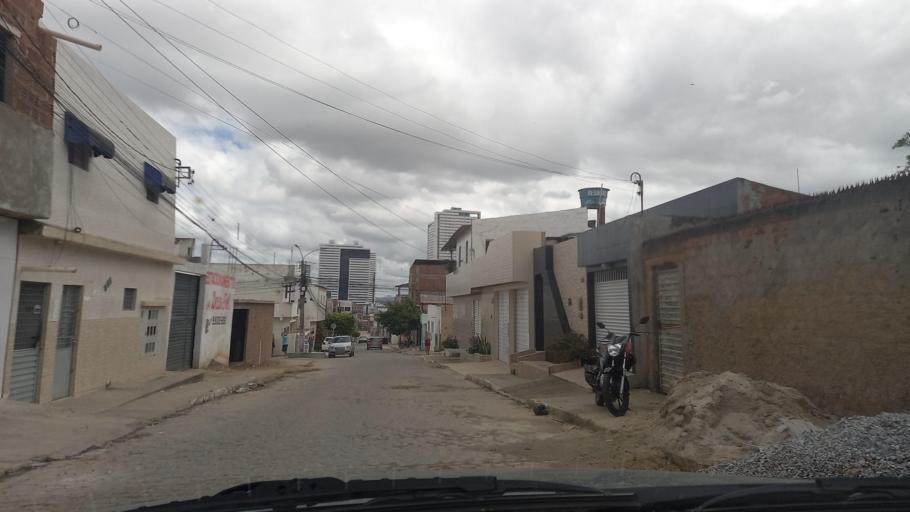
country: BR
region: Pernambuco
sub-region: Caruaru
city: Caruaru
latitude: -8.2664
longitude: -35.9567
